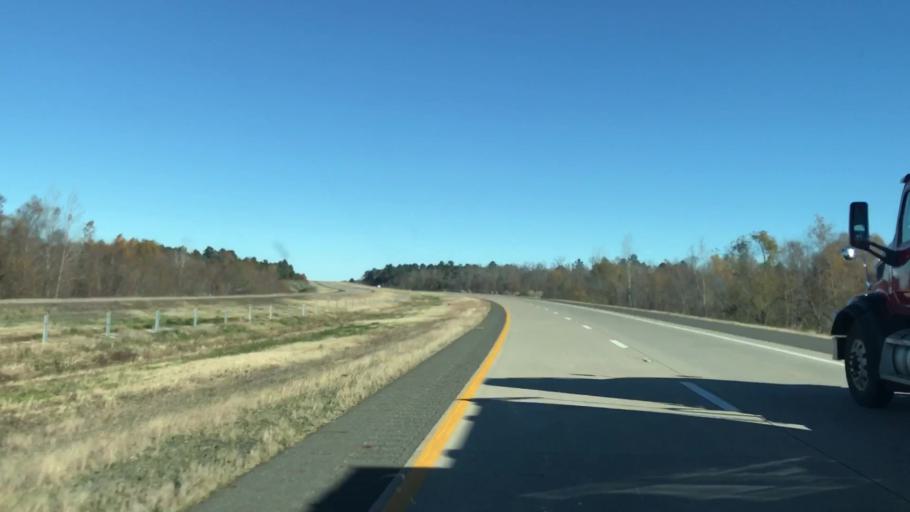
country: US
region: Texas
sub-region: Cass County
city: Queen City
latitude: 33.1693
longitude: -93.8781
